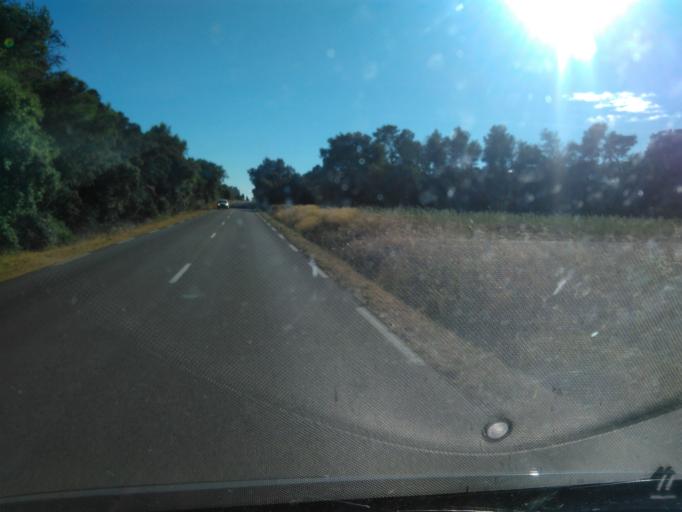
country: FR
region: Languedoc-Roussillon
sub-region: Departement du Gard
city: Beauvoisin
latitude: 43.6588
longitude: 4.3552
